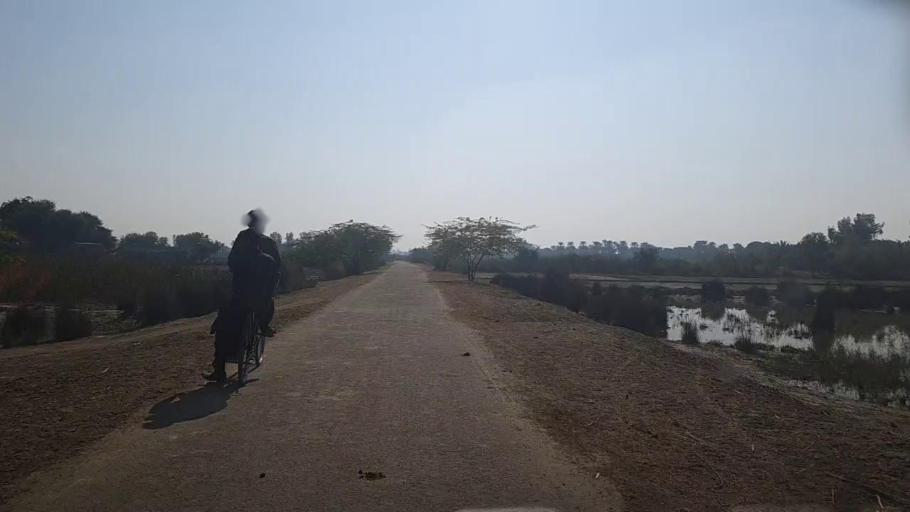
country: PK
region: Sindh
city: Kot Diji
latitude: 27.4273
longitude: 68.7372
